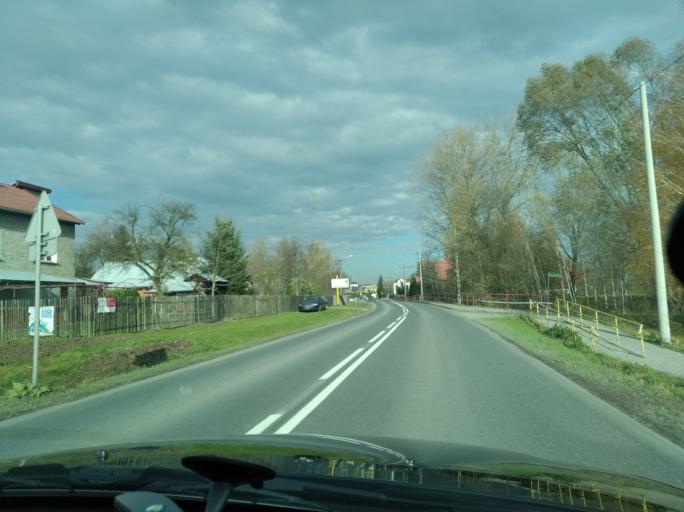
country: PL
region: Subcarpathian Voivodeship
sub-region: Powiat ropczycko-sedziszowski
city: Ostrow
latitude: 50.0949
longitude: 21.5935
